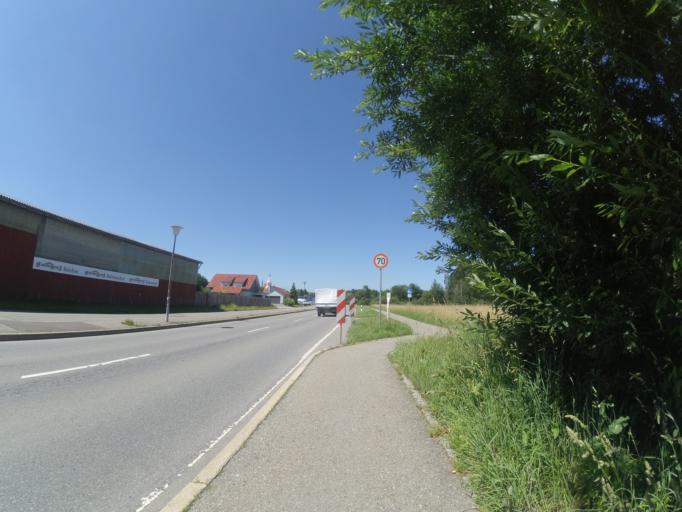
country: DE
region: Baden-Wuerttemberg
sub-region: Tuebingen Region
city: Bad Wurzach
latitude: 47.9122
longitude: 9.8896
